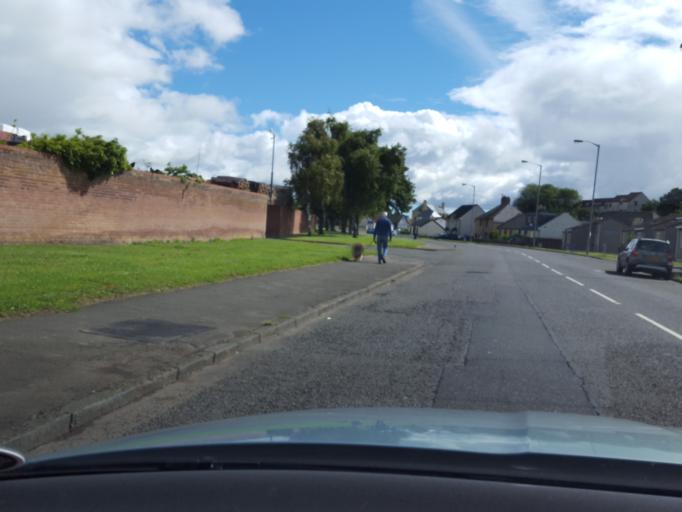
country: GB
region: Scotland
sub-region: Falkirk
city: Bo'ness
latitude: 56.0166
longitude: -3.5880
